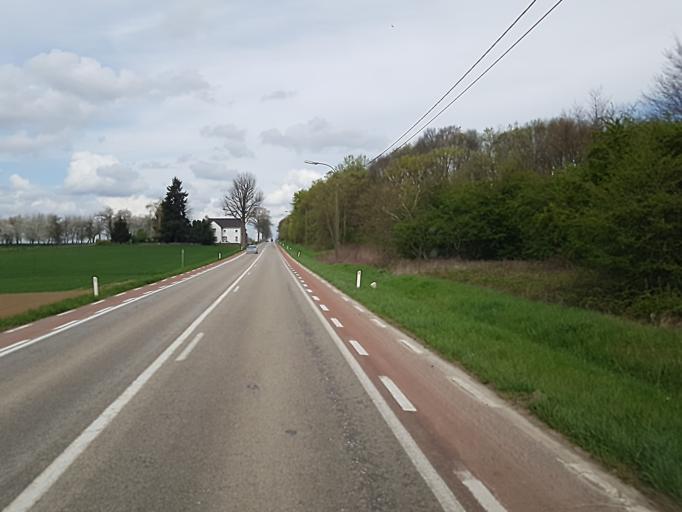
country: BE
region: Flanders
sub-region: Provincie Limburg
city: Riemst
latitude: 50.8484
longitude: 5.6253
